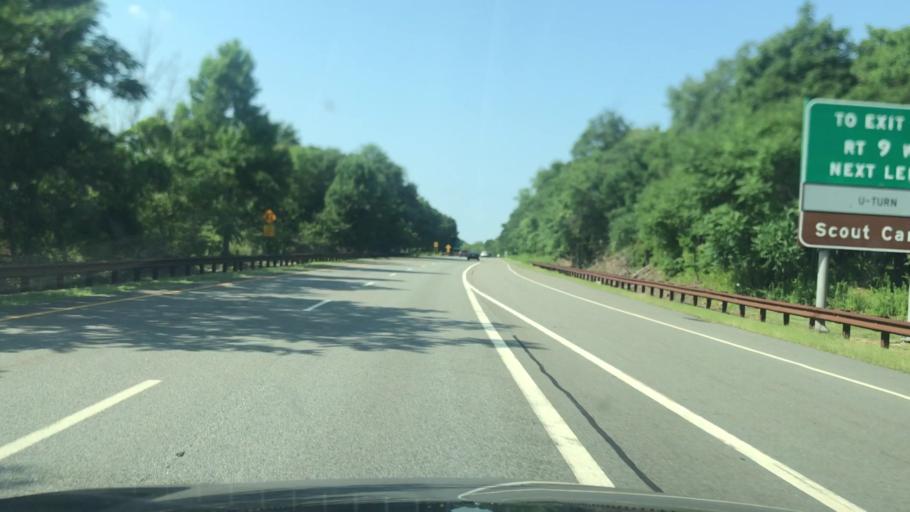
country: US
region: New Jersey
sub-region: Bergen County
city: Alpine
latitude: 40.9824
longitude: -73.9126
